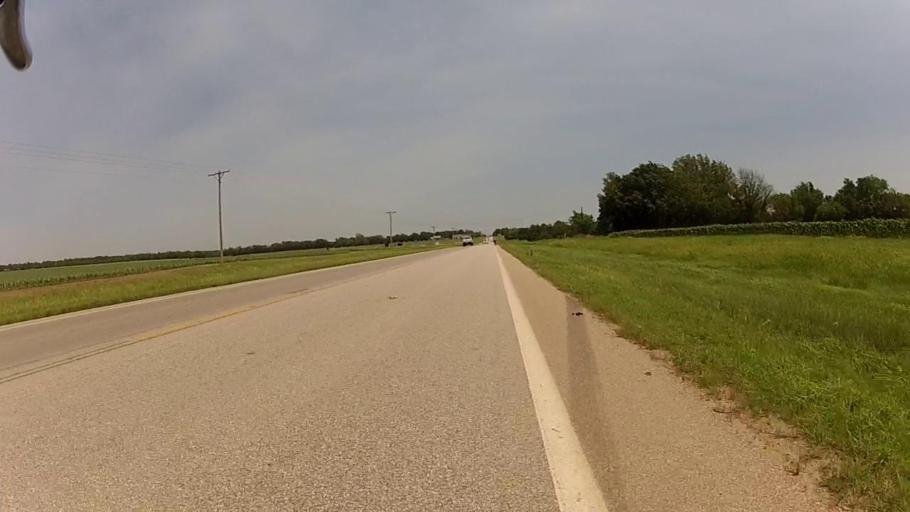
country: US
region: Kansas
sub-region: Cowley County
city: Arkansas City
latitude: 37.0565
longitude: -97.0925
